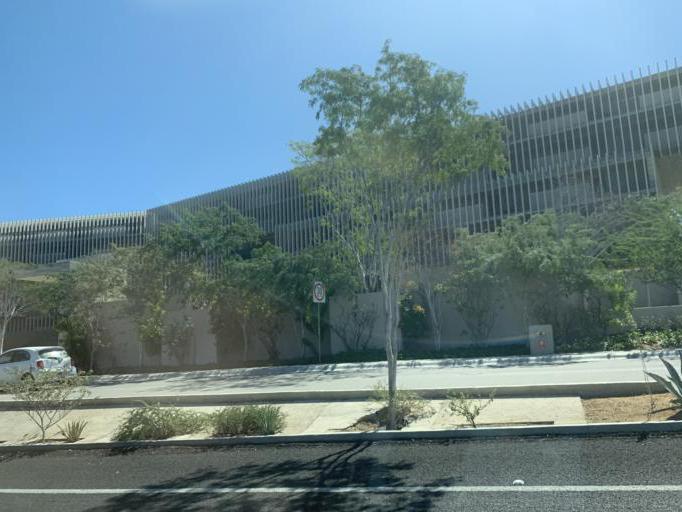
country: MX
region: Baja California Sur
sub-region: Los Cabos
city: San Jose del Cabo
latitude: 22.9741
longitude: -109.7824
